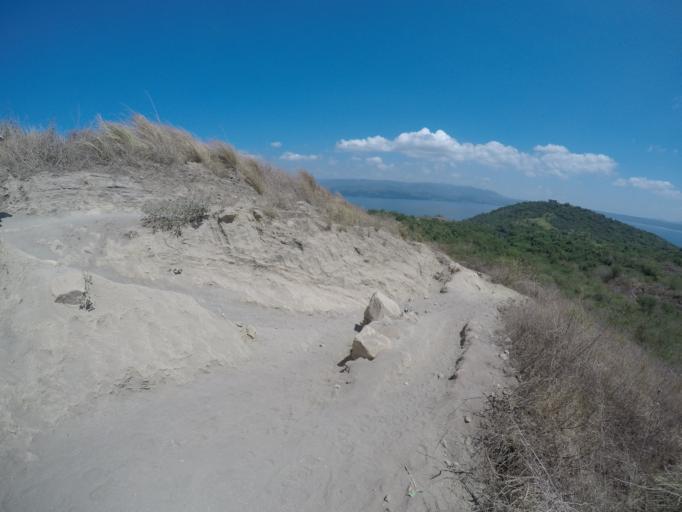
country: PH
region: Calabarzon
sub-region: Province of Batangas
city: Bugaan
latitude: 14.0196
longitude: 120.9995
